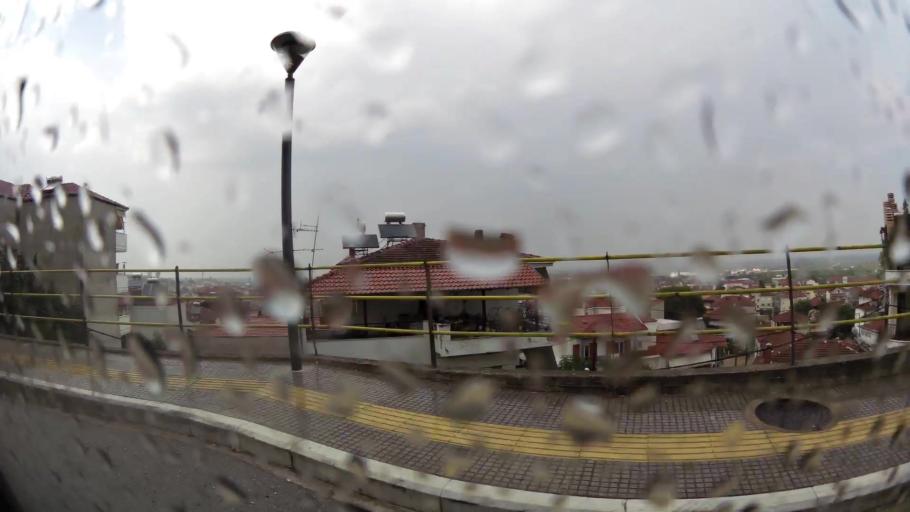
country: GR
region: Central Macedonia
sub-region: Nomos Imathias
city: Veroia
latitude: 40.5308
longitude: 22.2044
